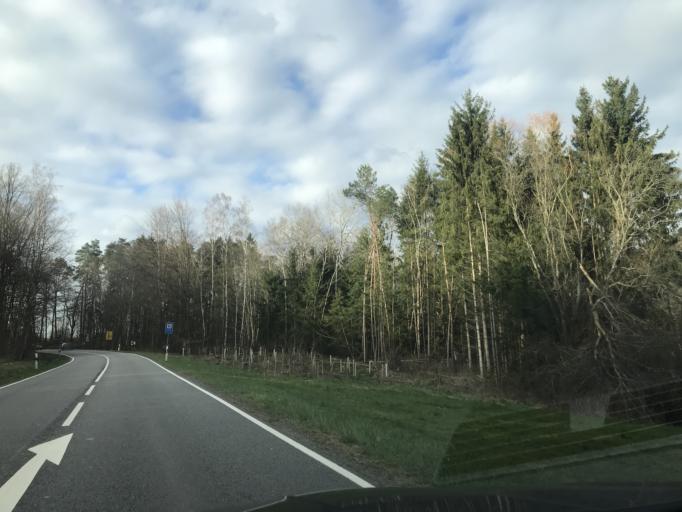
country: DE
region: Saarland
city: Kirkel
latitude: 49.2733
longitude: 7.2374
